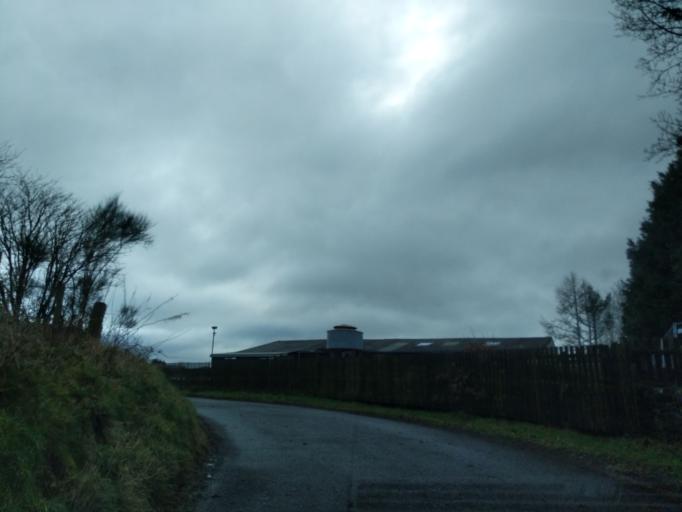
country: GB
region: Scotland
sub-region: Dumfries and Galloway
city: Moffat
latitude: 55.3213
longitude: -3.4298
